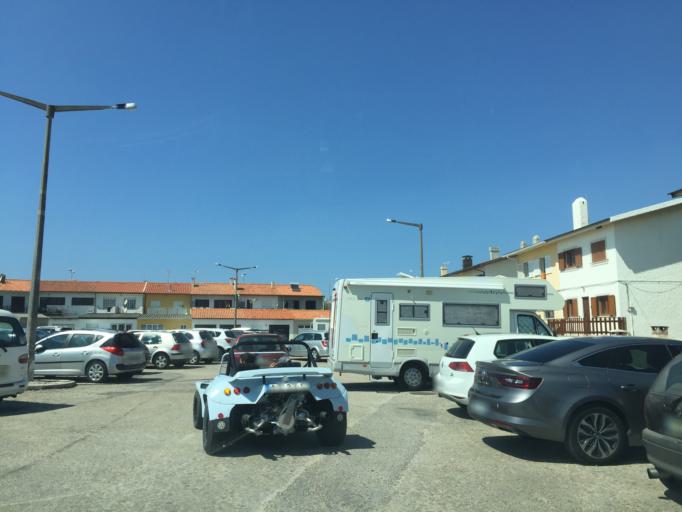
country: PT
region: Coimbra
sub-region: Mira
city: Mira
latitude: 40.3292
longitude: -8.8407
